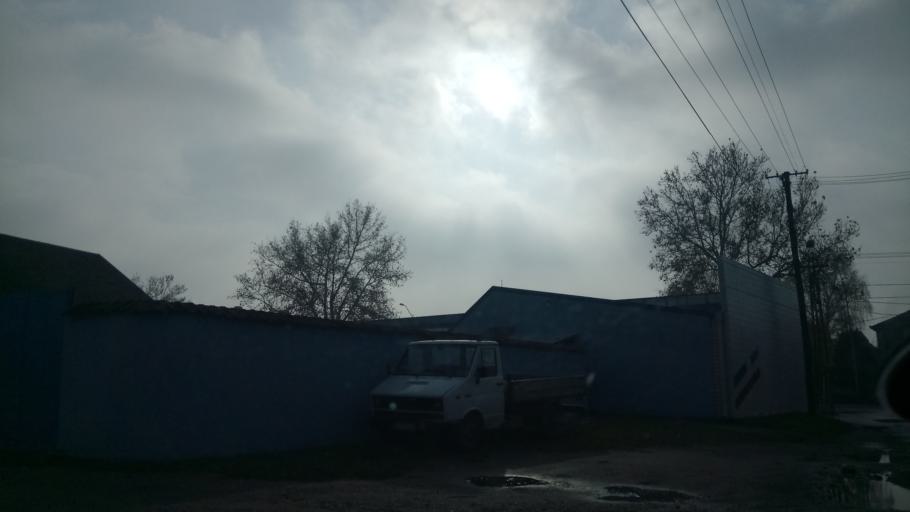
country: RS
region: Autonomna Pokrajina Vojvodina
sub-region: Sremski Okrug
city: Stara Pazova
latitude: 44.9758
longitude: 20.1701
